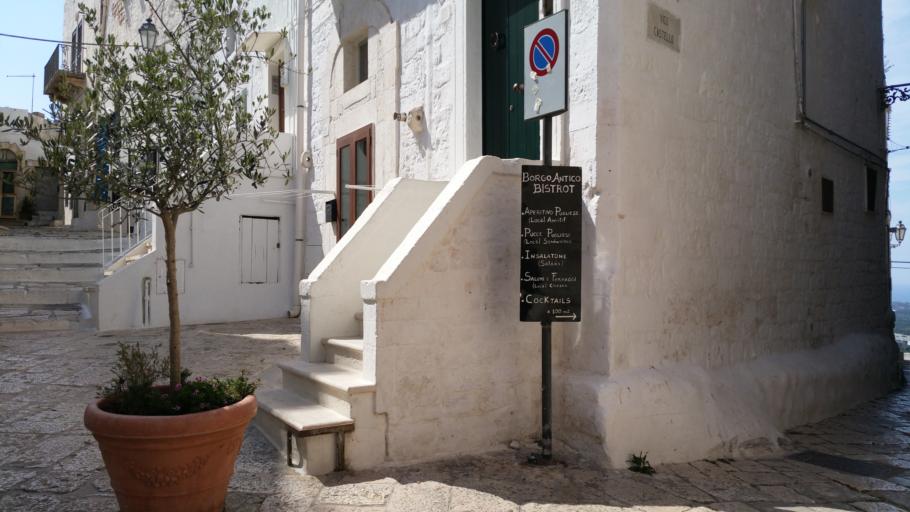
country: IT
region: Apulia
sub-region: Provincia di Brindisi
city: Ostuni
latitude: 40.7342
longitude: 17.5784
